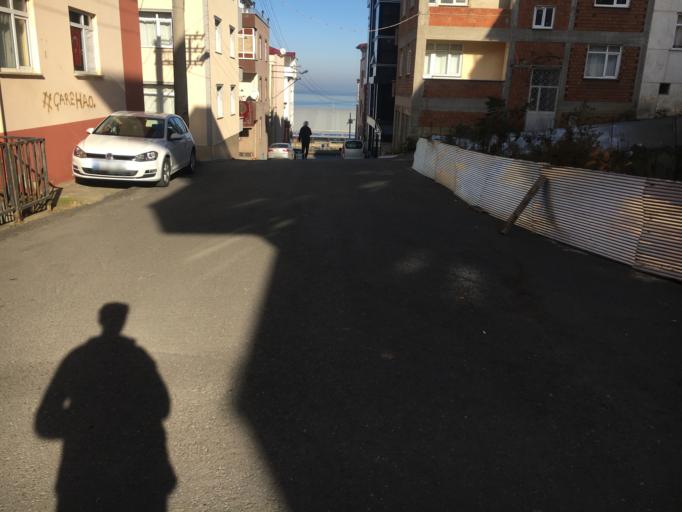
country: TR
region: Trabzon
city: Trabzon
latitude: 40.9933
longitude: 39.7787
